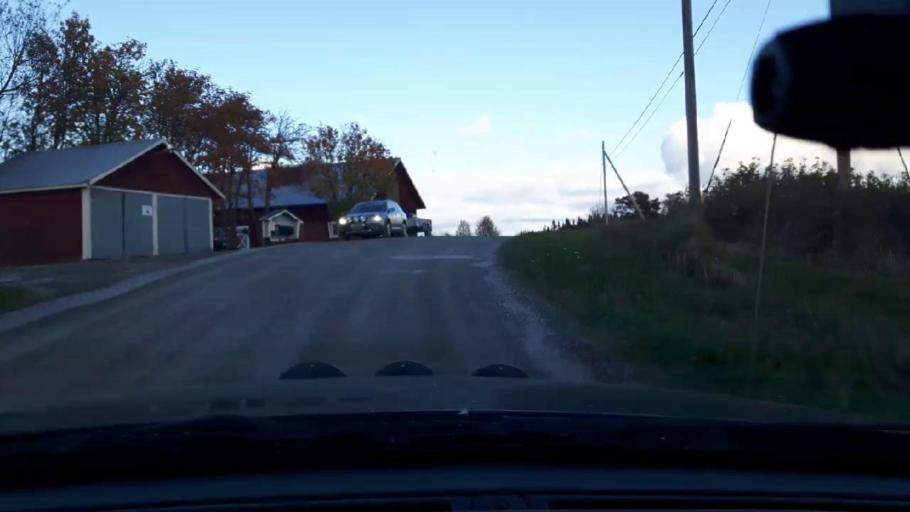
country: SE
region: Jaemtland
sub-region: Krokoms Kommun
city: Krokom
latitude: 63.0794
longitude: 14.2767
